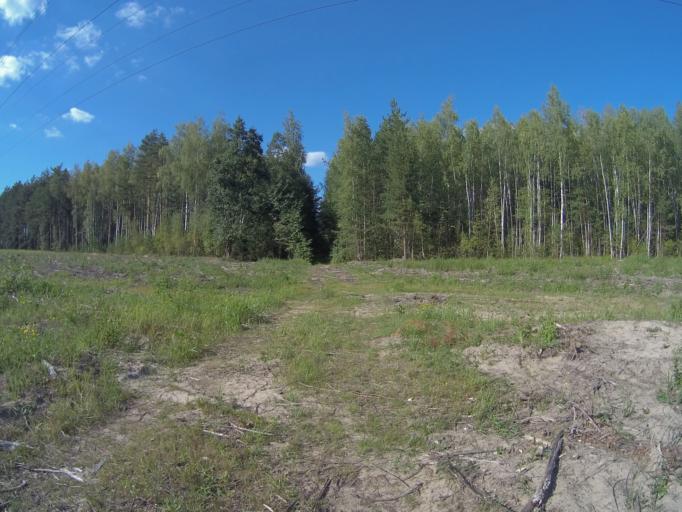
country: RU
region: Vladimir
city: Kommunar
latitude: 56.0614
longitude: 40.4470
